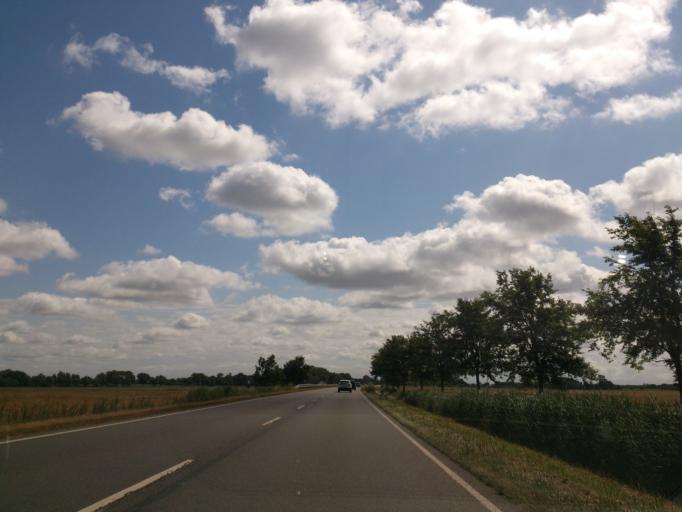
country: DE
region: Schleswig-Holstein
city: Grothusenkoog
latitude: 54.3072
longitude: 8.7457
